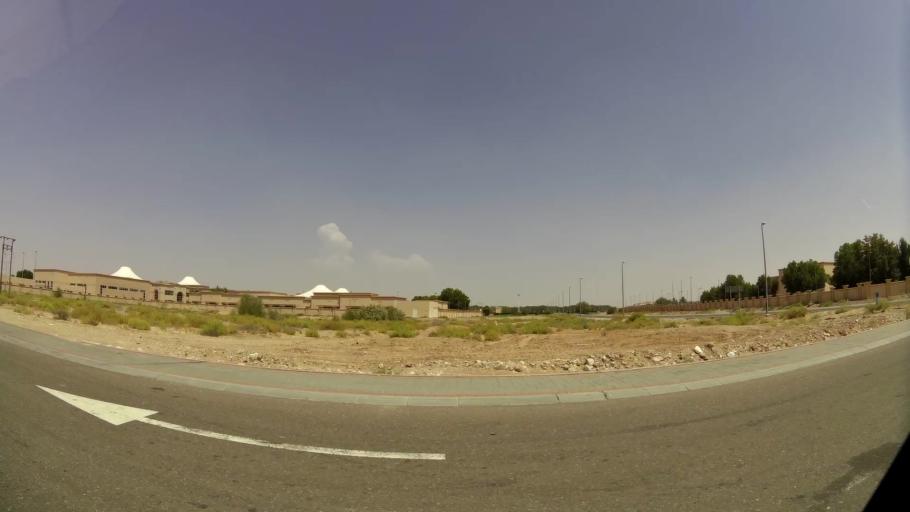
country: AE
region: Abu Dhabi
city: Al Ain
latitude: 24.2596
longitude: 55.6894
